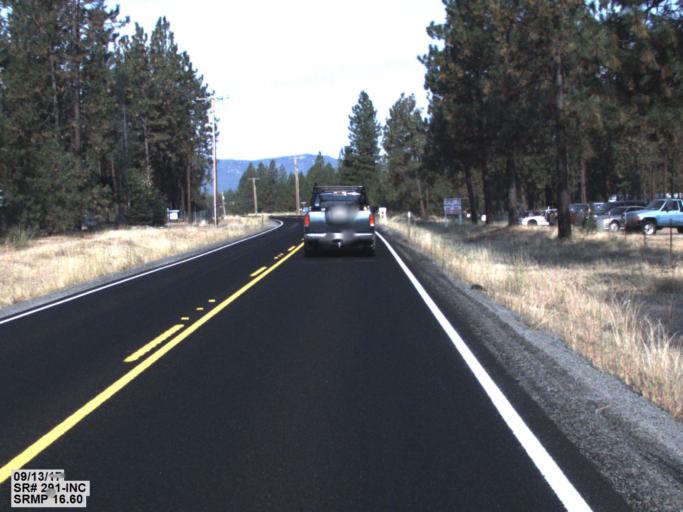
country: US
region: Washington
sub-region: Spokane County
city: Deer Park
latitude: 47.8428
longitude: -117.6189
